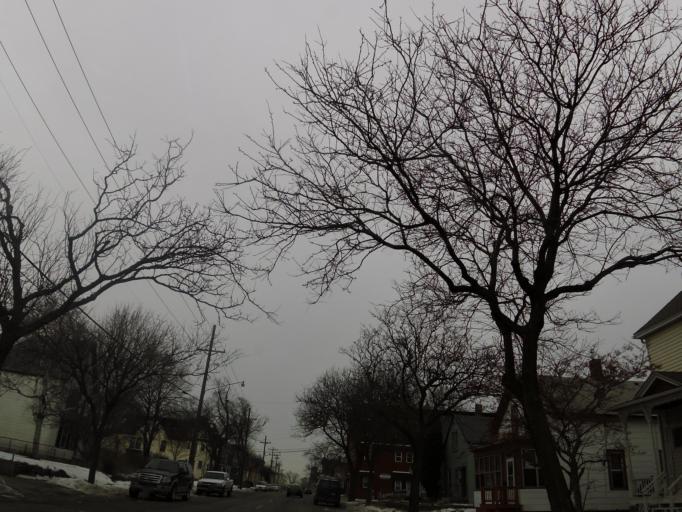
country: US
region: Minnesota
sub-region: Ramsey County
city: Saint Paul
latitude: 44.9557
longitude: -93.0712
